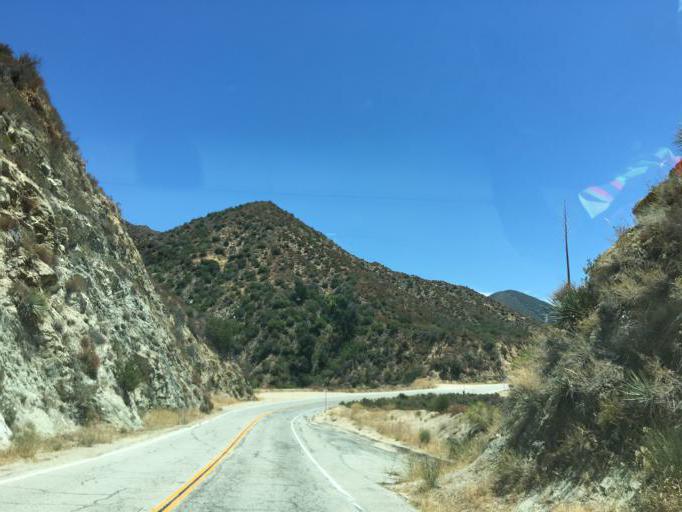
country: US
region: California
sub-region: Los Angeles County
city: La Crescenta-Montrose
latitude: 34.2897
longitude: -118.2277
